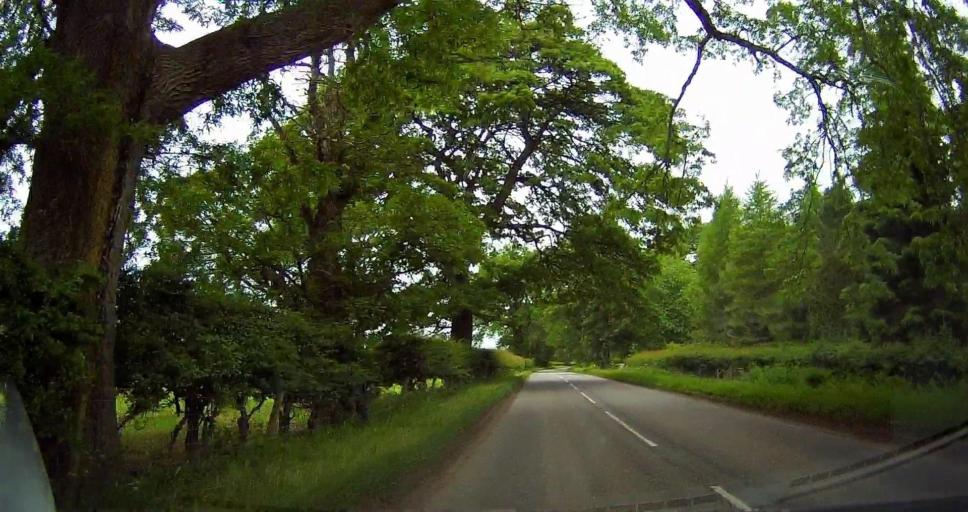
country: GB
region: Scotland
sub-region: Highland
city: Dornoch
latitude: 57.9769
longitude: -4.1069
